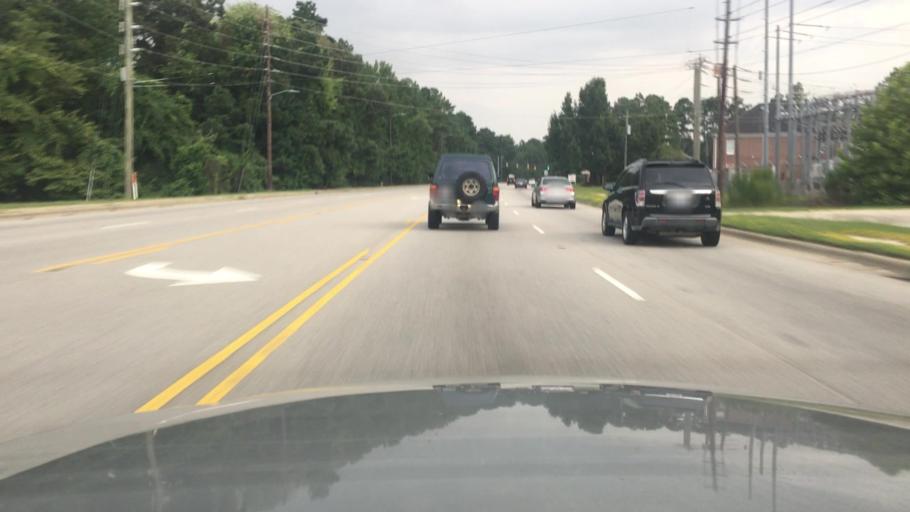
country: US
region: North Carolina
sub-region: Cumberland County
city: Fort Bragg
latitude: 35.0802
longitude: -79.0101
